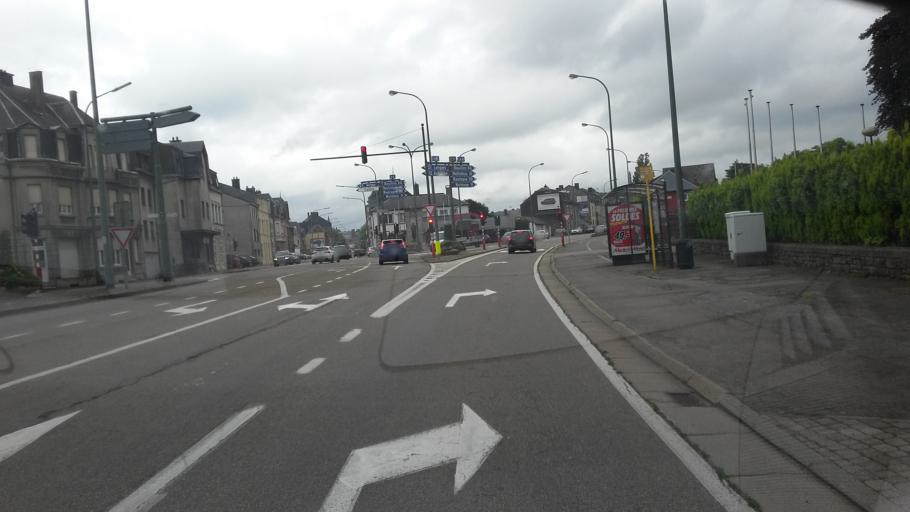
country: BE
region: Wallonia
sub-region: Province du Luxembourg
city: Arlon
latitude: 49.6747
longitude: 5.8246
